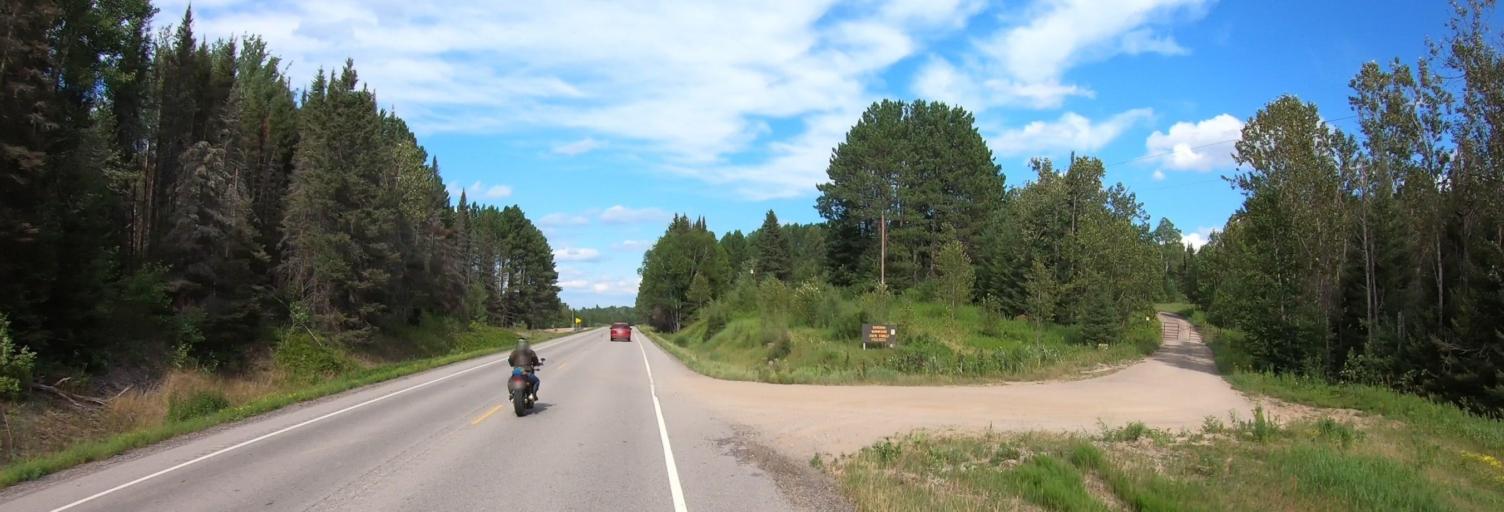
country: US
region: Minnesota
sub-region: Saint Louis County
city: Ely
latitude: 47.8887
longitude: -91.9419
